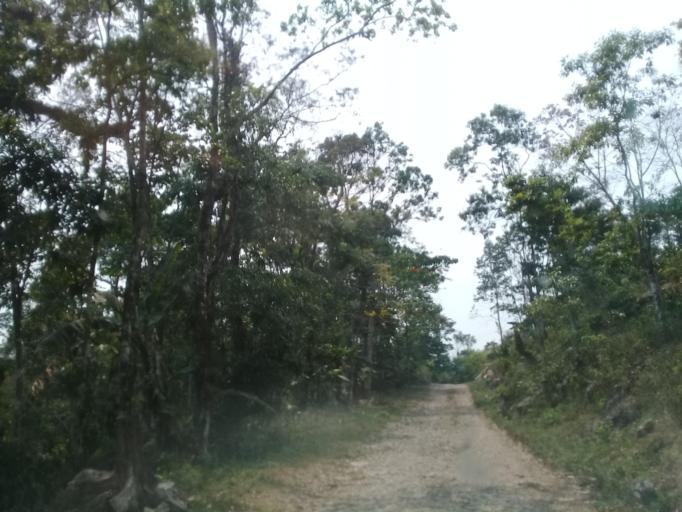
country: MX
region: Veracruz
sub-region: Tezonapa
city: Laguna Chica (Pueblo Nuevo)
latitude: 18.5808
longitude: -96.7544
